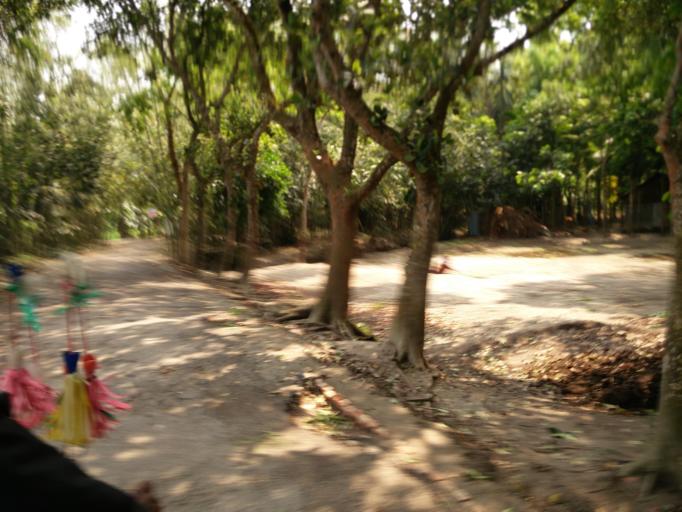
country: BD
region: Dhaka
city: Sherpur
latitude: 24.9348
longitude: 90.1593
